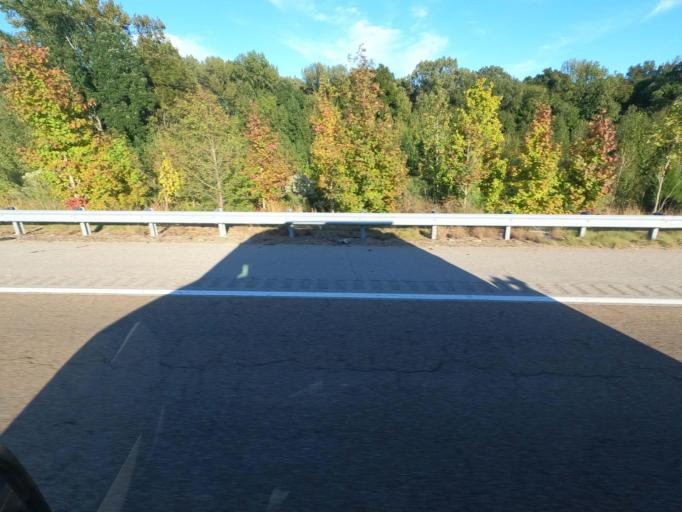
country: US
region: Tennessee
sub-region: Fayette County
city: Hickory Withe
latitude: 35.1991
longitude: -89.6523
